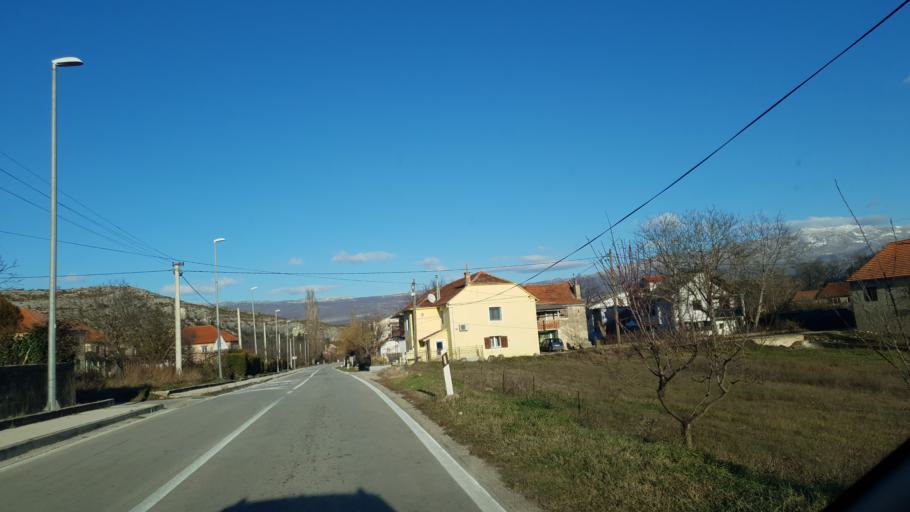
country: HR
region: Splitsko-Dalmatinska
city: Sinj
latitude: 43.7149
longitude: 16.6629
